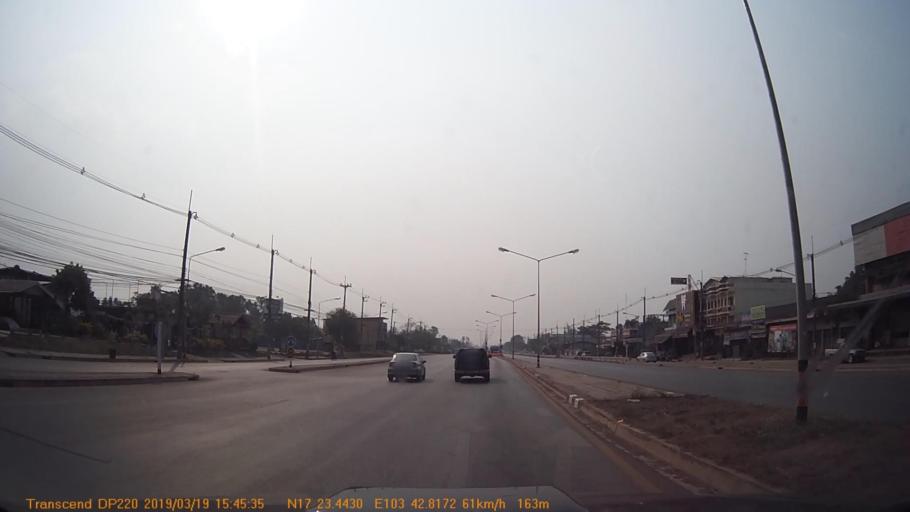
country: TH
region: Sakon Nakhon
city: Phang Khon
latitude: 17.3908
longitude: 103.7134
